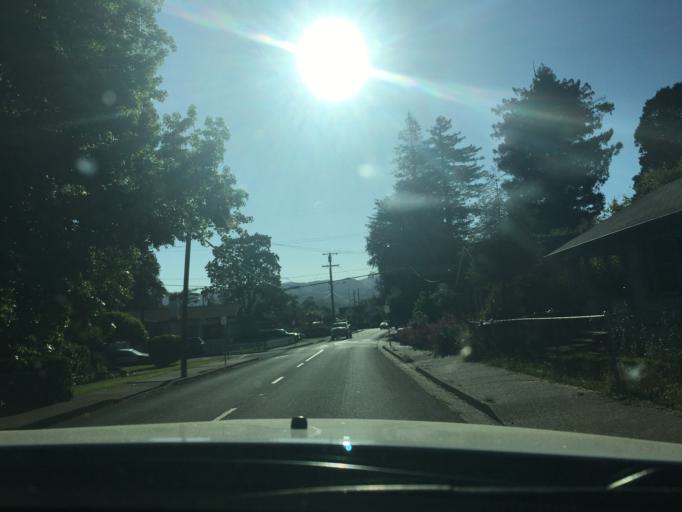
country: US
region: California
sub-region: Mendocino County
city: Ukiah
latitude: 39.1536
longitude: -123.2101
